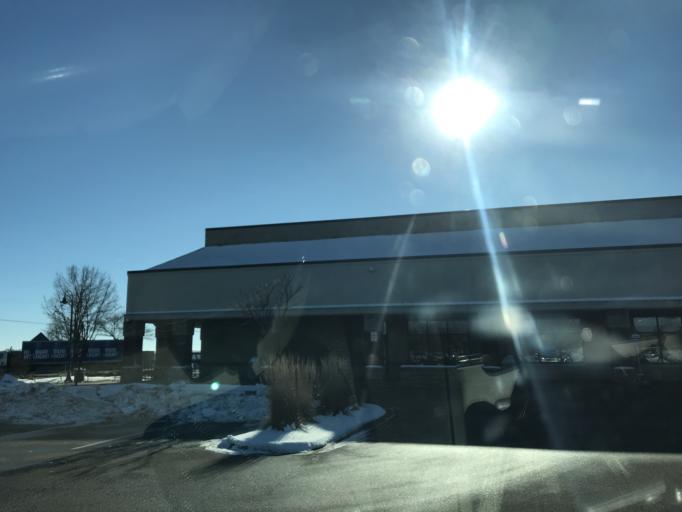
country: US
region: Wisconsin
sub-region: Dane County
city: Monona
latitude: 43.0463
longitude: -89.3223
